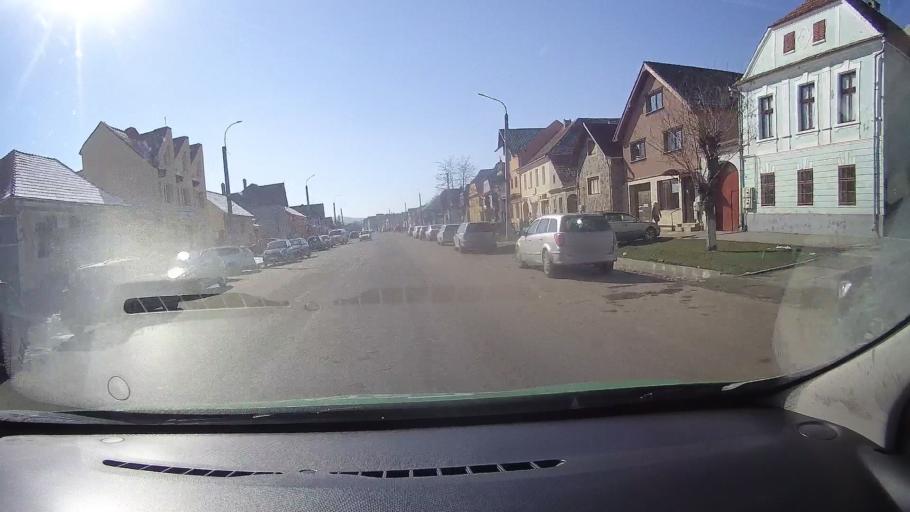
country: RO
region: Brasov
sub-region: Oras Rupea
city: Rupea
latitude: 46.0369
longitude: 25.2190
